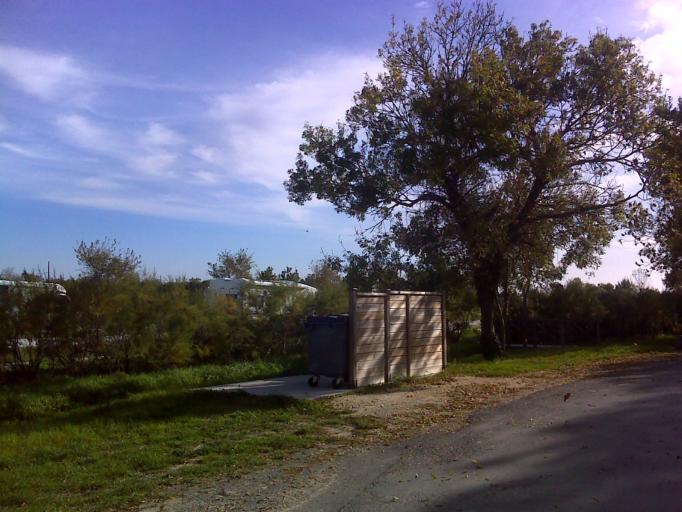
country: FR
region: Poitou-Charentes
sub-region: Departement de la Charente-Maritime
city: Marennes
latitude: 45.8684
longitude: -1.0690
